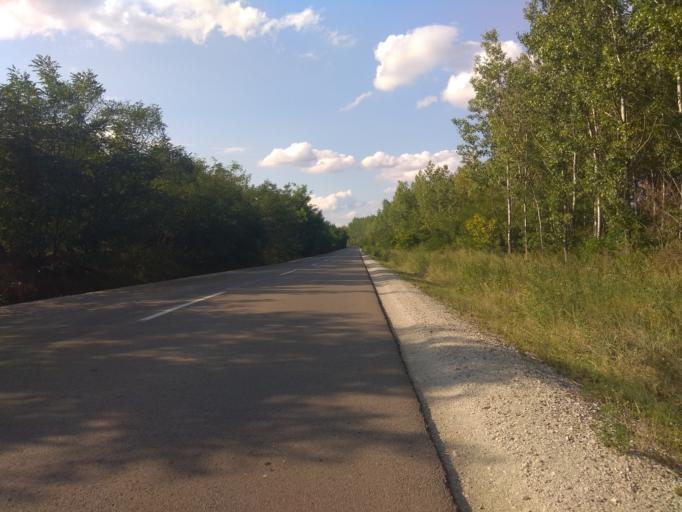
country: HU
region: Borsod-Abauj-Zemplen
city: Hejobaba
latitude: 47.8858
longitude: 20.8976
